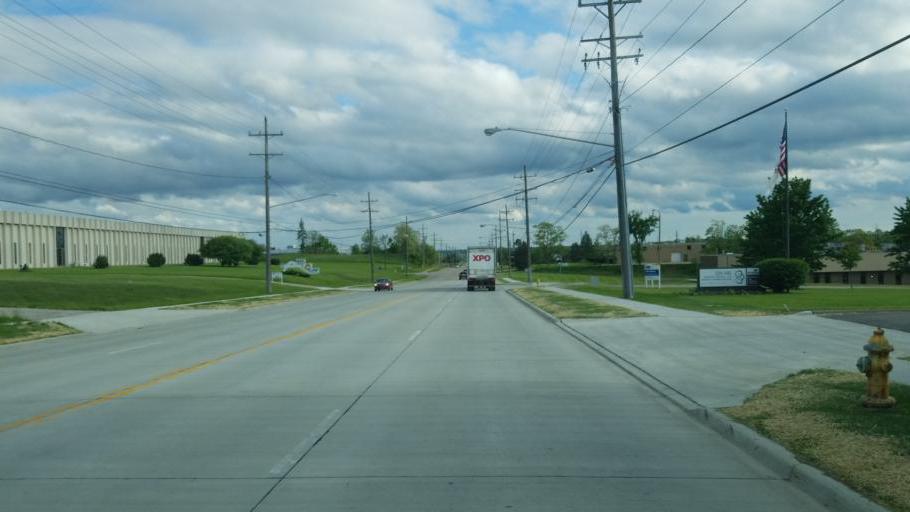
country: US
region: Ohio
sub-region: Cuyahoga County
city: Solon
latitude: 41.3750
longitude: -81.4695
